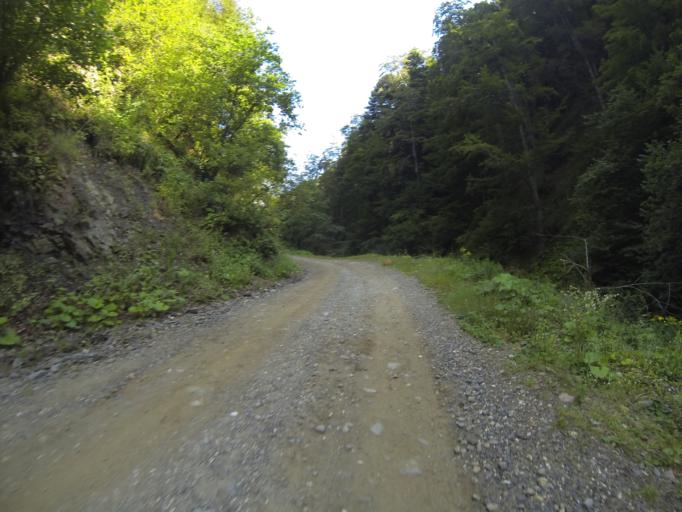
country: RO
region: Valcea
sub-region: Comuna Costesti
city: Bistrita
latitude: 45.2386
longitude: 24.0021
